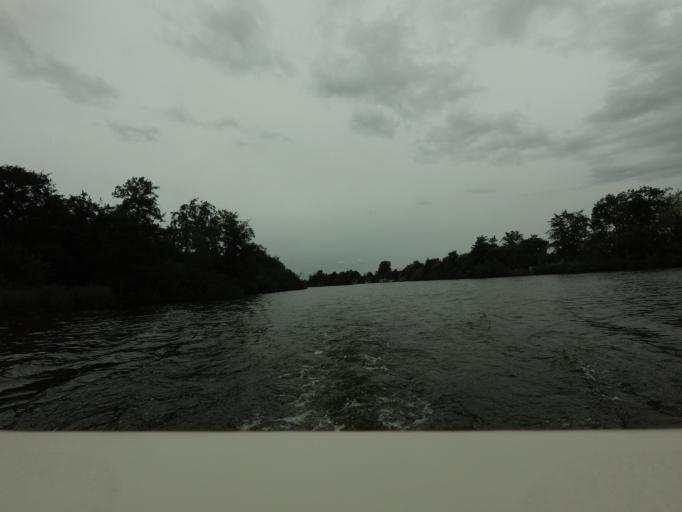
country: NL
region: Friesland
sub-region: Gemeente Tytsjerksteradiel
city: Garyp
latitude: 53.1204
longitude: 5.9438
